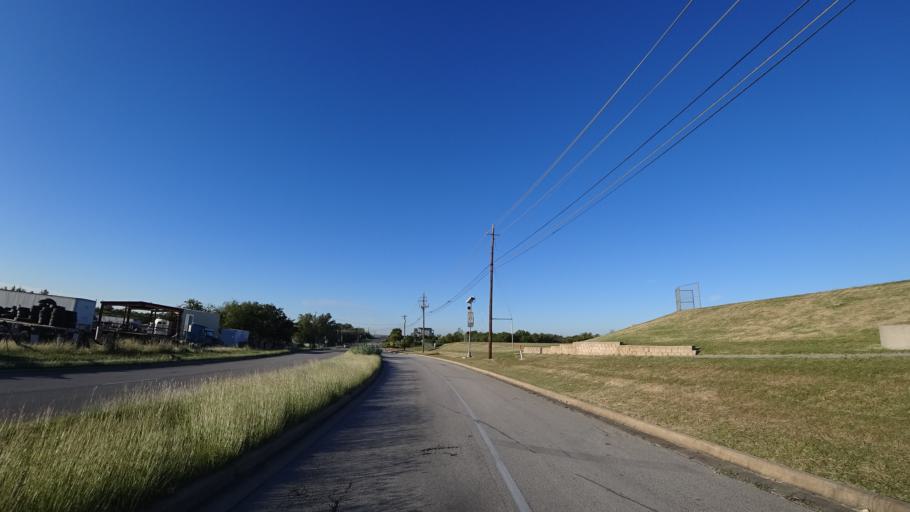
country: US
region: Texas
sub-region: Travis County
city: Hornsby Bend
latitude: 30.3090
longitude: -97.6427
